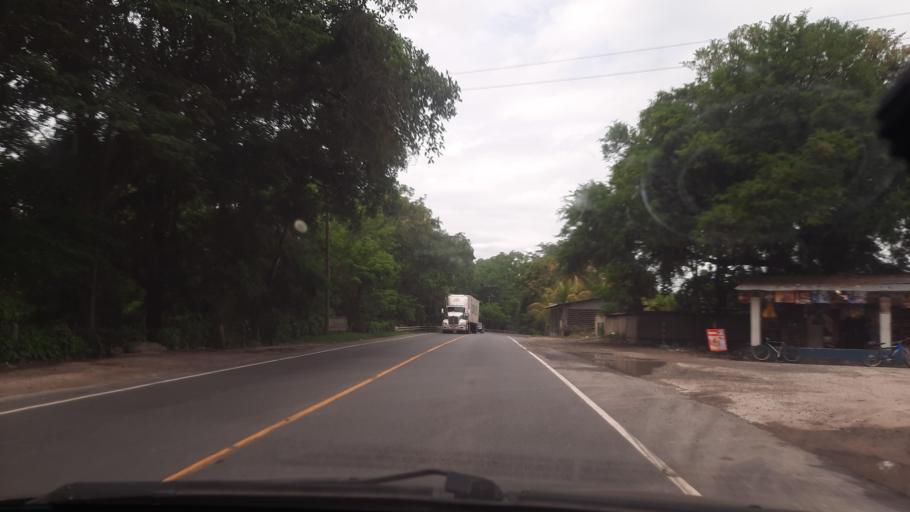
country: GT
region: Izabal
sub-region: Municipio de Los Amates
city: Los Amates
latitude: 15.2407
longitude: -89.1722
